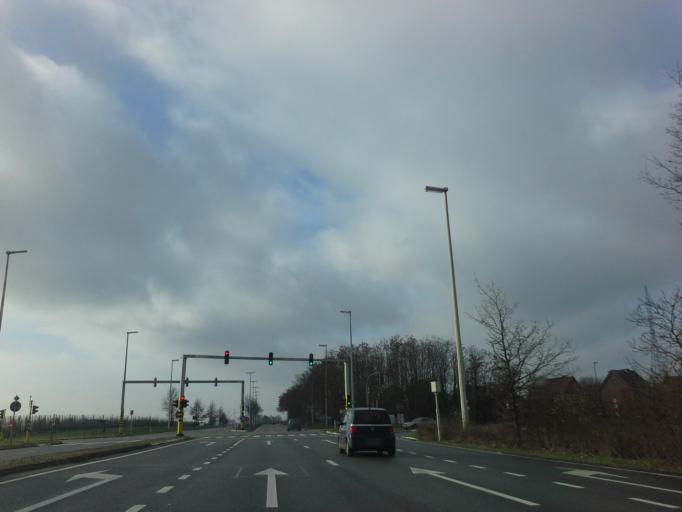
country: BE
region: Flanders
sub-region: Provincie Limburg
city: Nieuwerkerken
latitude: 50.8541
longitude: 5.2453
